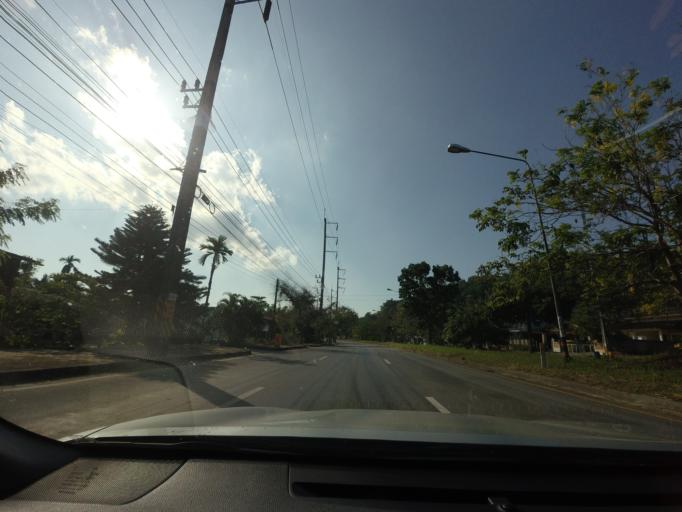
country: TH
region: Phangnga
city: Thai Mueang
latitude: 8.2725
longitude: 98.3255
